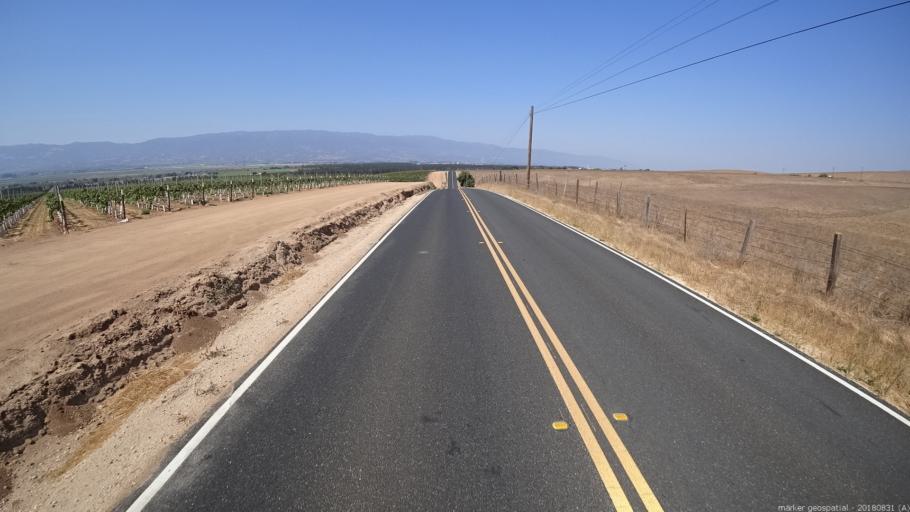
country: US
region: California
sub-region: Monterey County
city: Soledad
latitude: 36.4159
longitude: -121.2703
